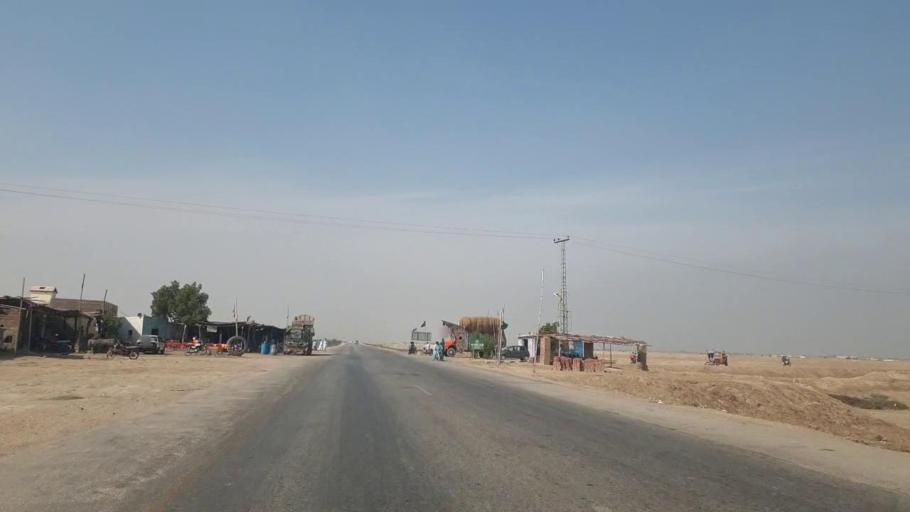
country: PK
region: Sindh
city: Sann
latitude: 25.9021
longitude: 68.2315
